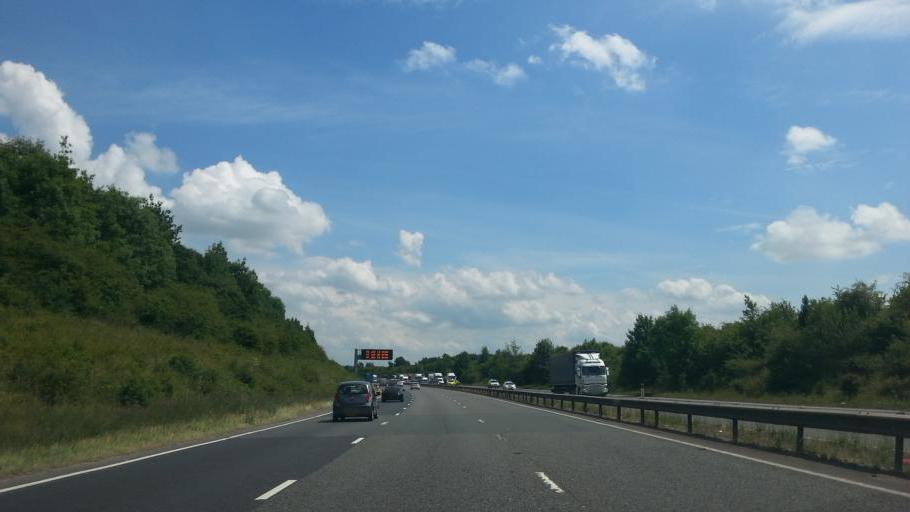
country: GB
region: England
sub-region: Suffolk
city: Newmarket
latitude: 52.2675
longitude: 0.4208
